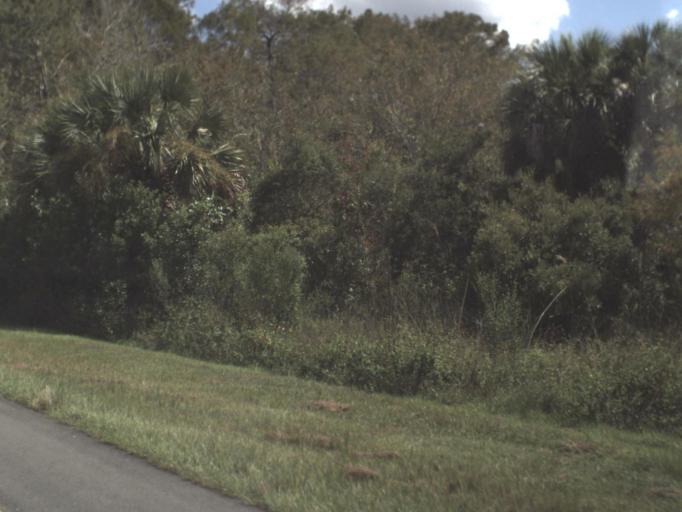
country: US
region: Florida
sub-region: Collier County
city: Marco
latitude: 25.8720
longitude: -81.1827
